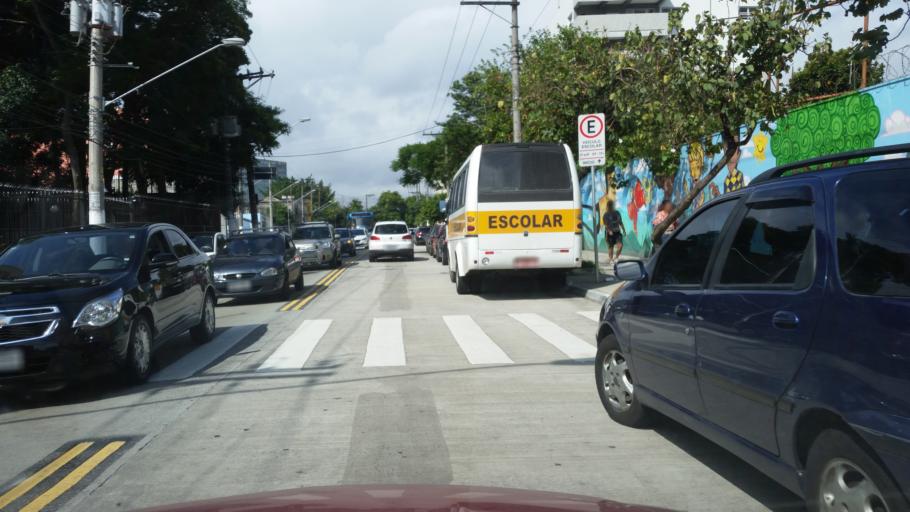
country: BR
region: Sao Paulo
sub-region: Diadema
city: Diadema
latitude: -23.6599
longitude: -46.7071
